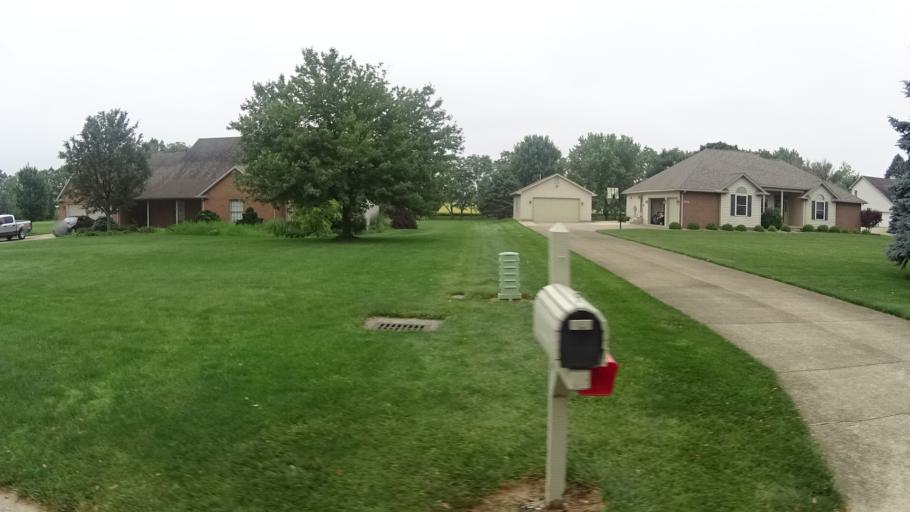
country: US
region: Ohio
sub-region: Erie County
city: Huron
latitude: 41.3582
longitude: -82.5718
